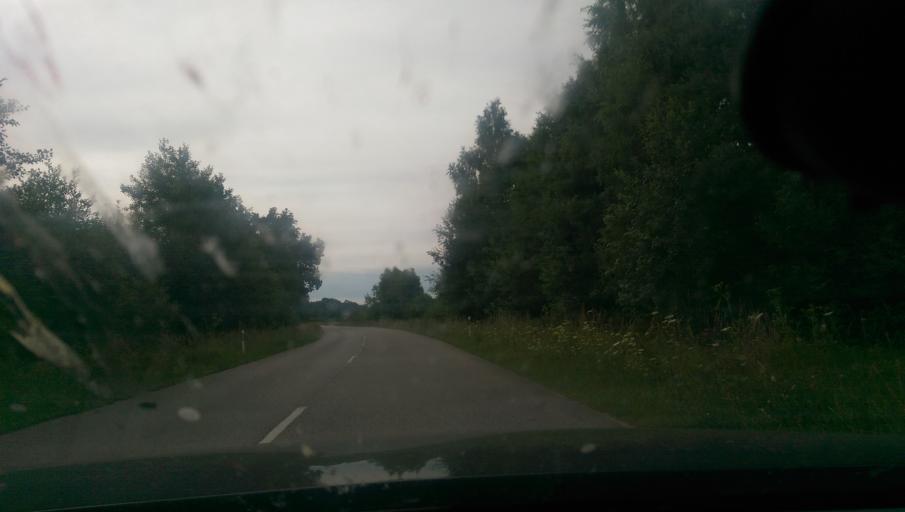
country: LT
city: Priekule
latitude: 55.6021
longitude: 21.3972
